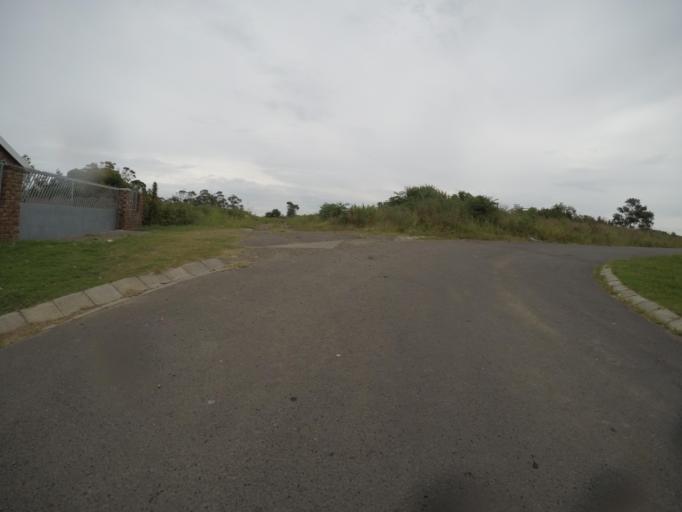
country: ZA
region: Eastern Cape
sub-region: Buffalo City Metropolitan Municipality
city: East London
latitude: -33.0013
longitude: 27.8505
